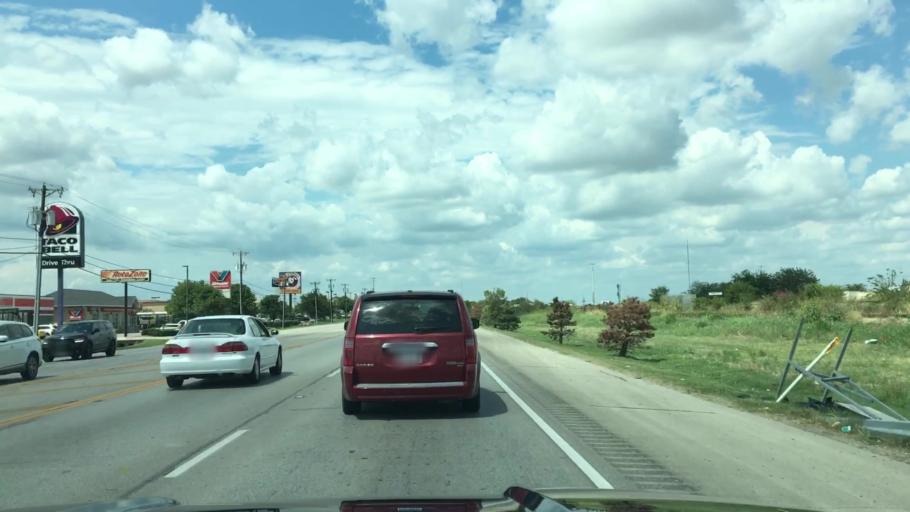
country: US
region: Texas
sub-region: Tarrant County
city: Saginaw
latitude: 32.8774
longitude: -97.3787
